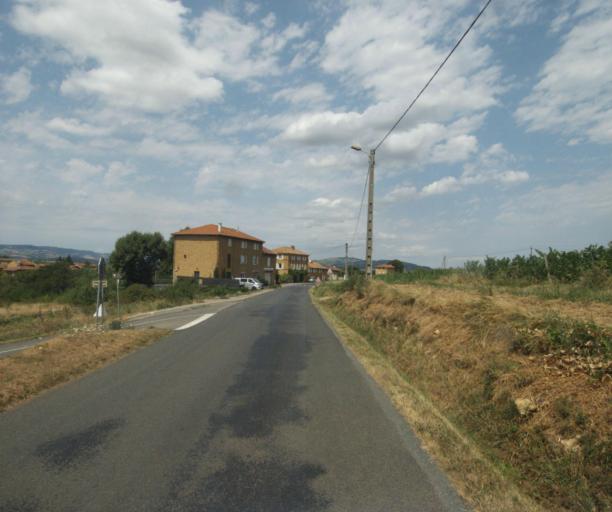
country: FR
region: Rhone-Alpes
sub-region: Departement du Rhone
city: Chatillon
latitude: 45.8736
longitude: 4.6040
